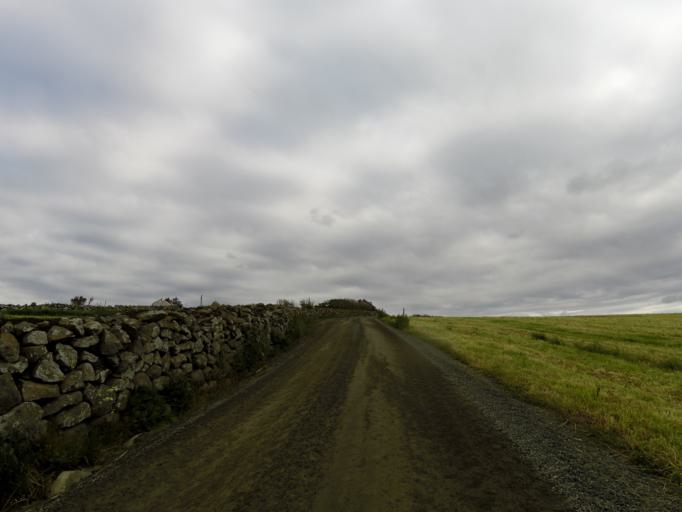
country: NO
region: Vest-Agder
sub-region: Farsund
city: Vestbygd
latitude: 58.1366
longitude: 6.6062
